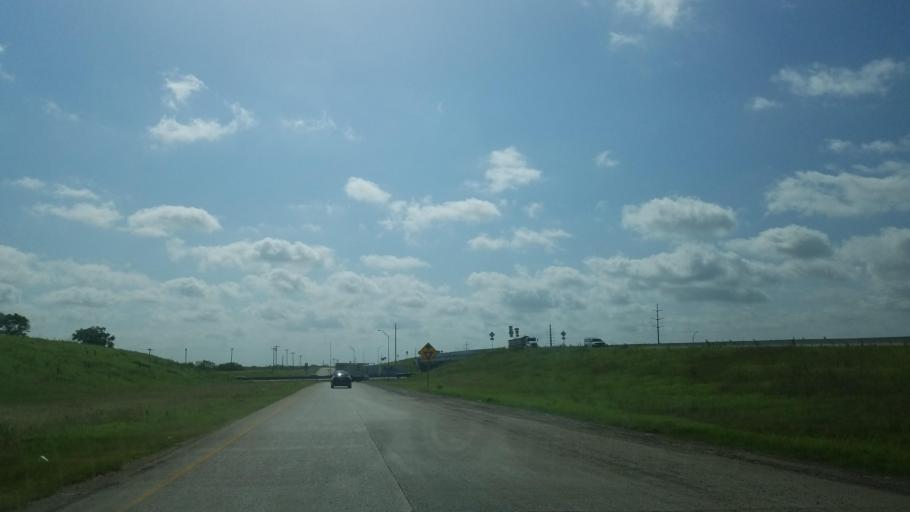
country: US
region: Texas
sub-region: Denton County
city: Krum
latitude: 33.2562
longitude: -97.1801
